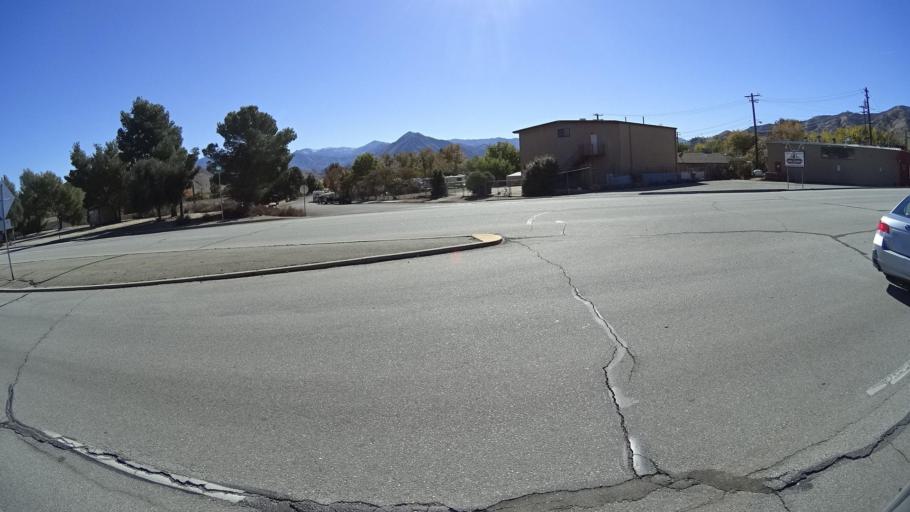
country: US
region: California
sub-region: Kern County
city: Wofford Heights
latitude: 35.7084
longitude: -118.4529
